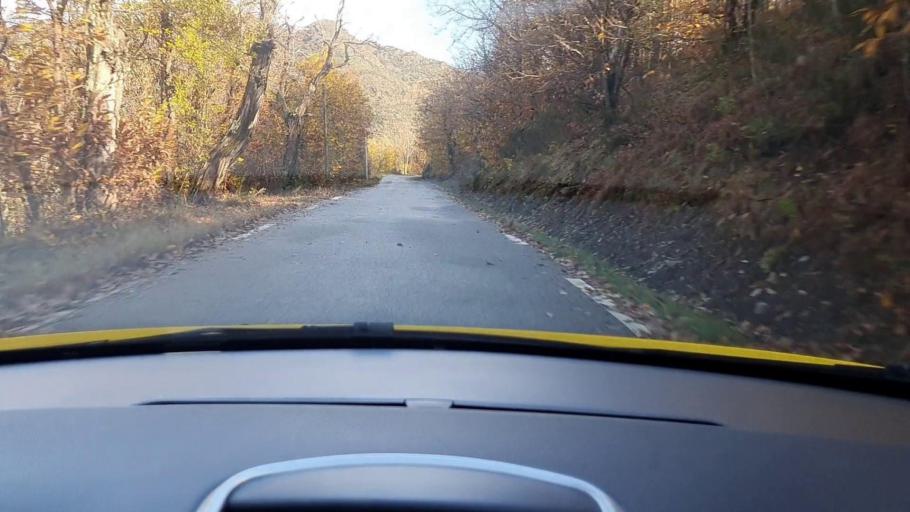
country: FR
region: Languedoc-Roussillon
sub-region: Departement du Gard
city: Valleraugue
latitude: 44.1647
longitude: 3.6486
